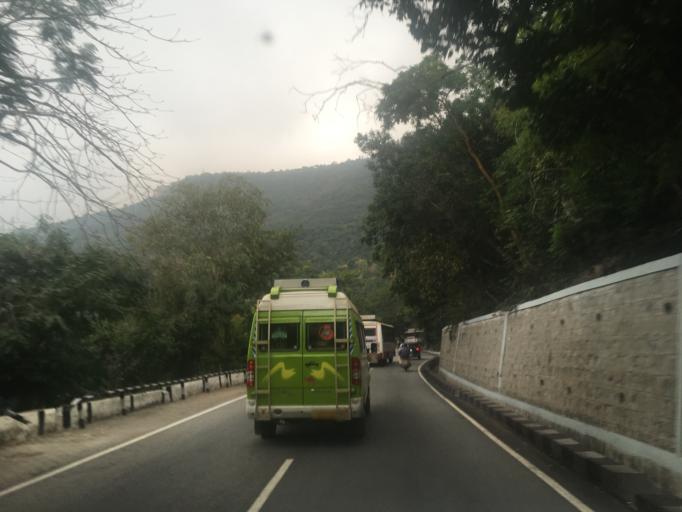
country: IN
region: Andhra Pradesh
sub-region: Chittoor
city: Tirumala
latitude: 13.6608
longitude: 79.3500
